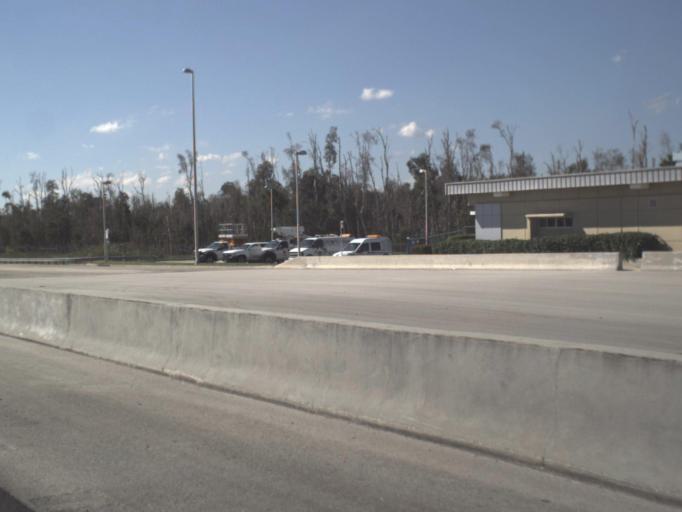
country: US
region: Florida
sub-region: Miami-Dade County
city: Doral
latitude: 25.8488
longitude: -80.3876
